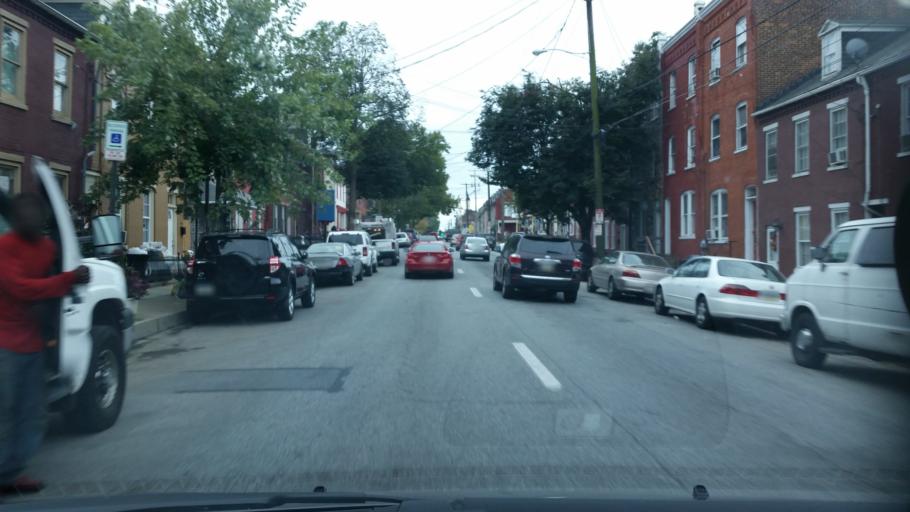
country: US
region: Pennsylvania
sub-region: Lancaster County
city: Lancaster
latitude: 40.0321
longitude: -76.3067
